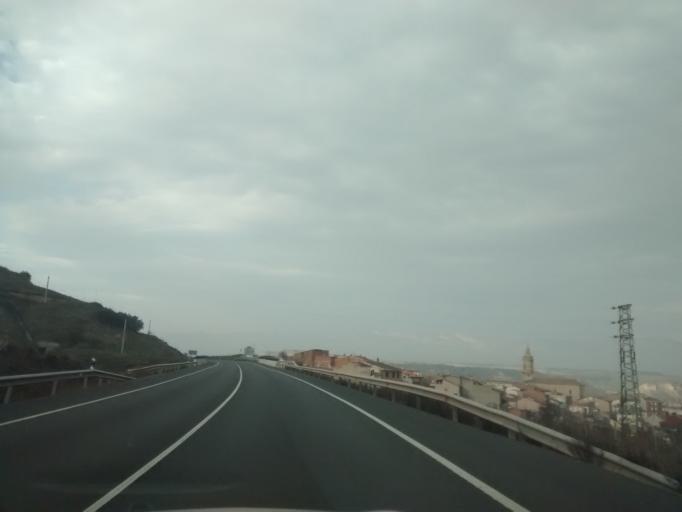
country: ES
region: La Rioja
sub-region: Provincia de La Rioja
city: Cenicero
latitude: 42.4775
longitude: -2.6431
